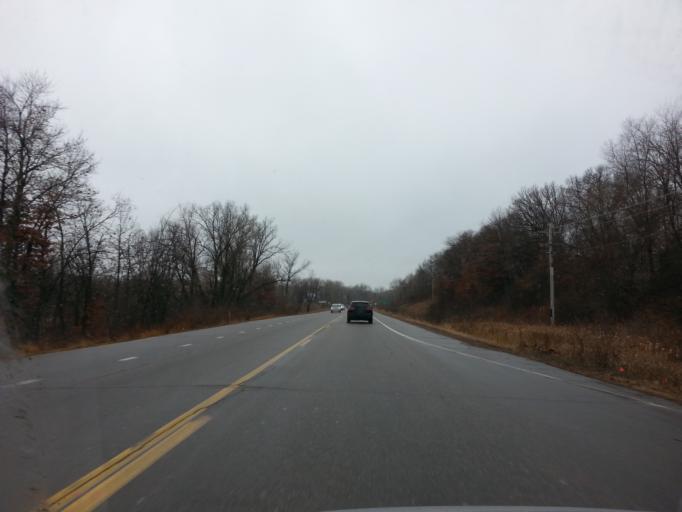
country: US
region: Minnesota
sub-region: Scott County
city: Prior Lake
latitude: 44.7373
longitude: -93.3837
